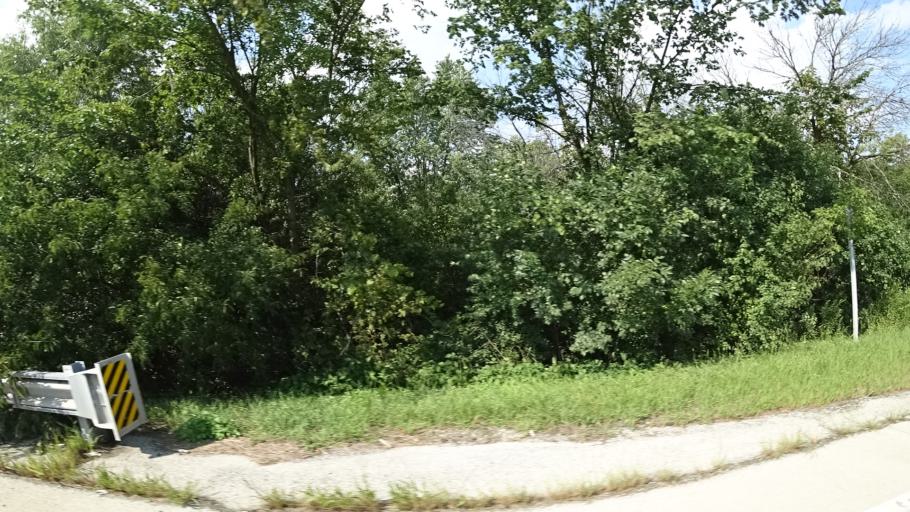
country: US
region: Illinois
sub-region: Will County
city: Goodings Grove
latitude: 41.6515
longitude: -87.8967
